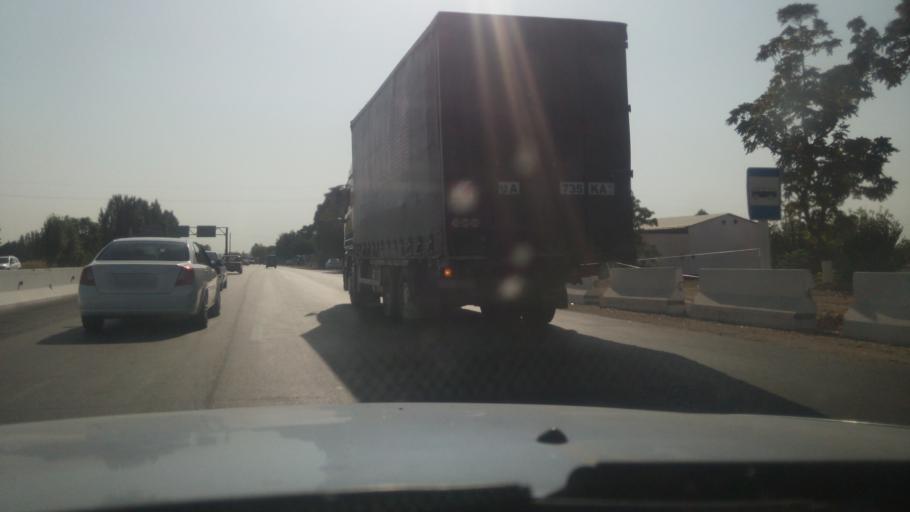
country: UZ
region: Toshkent
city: Urtaowul
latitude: 41.2208
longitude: 69.1363
